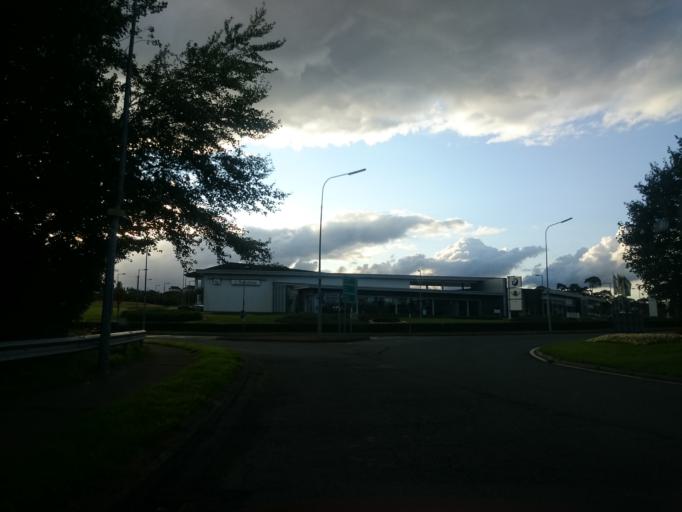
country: IE
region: Leinster
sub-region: Loch Garman
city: Enniscorthy
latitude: 52.5136
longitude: -6.5644
